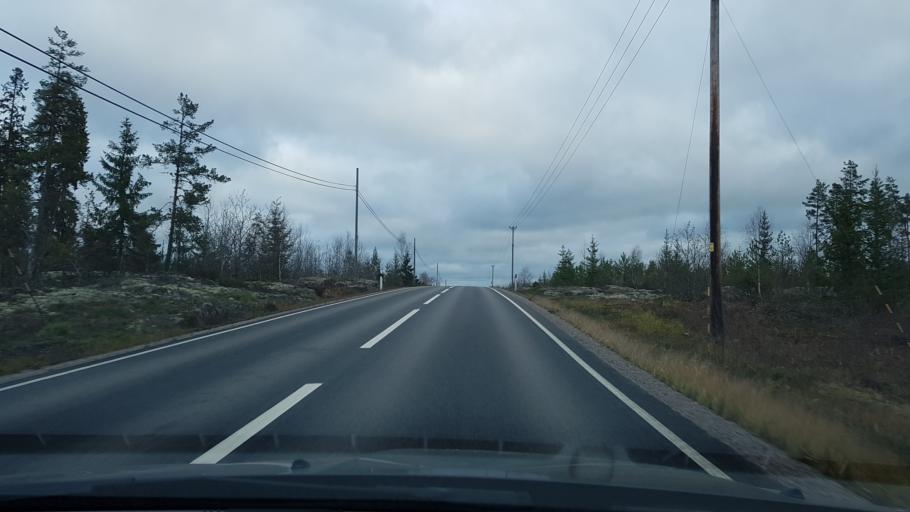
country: SE
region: Stockholm
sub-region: Norrtalje Kommun
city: Nykvarn
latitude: 59.9966
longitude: 18.2943
